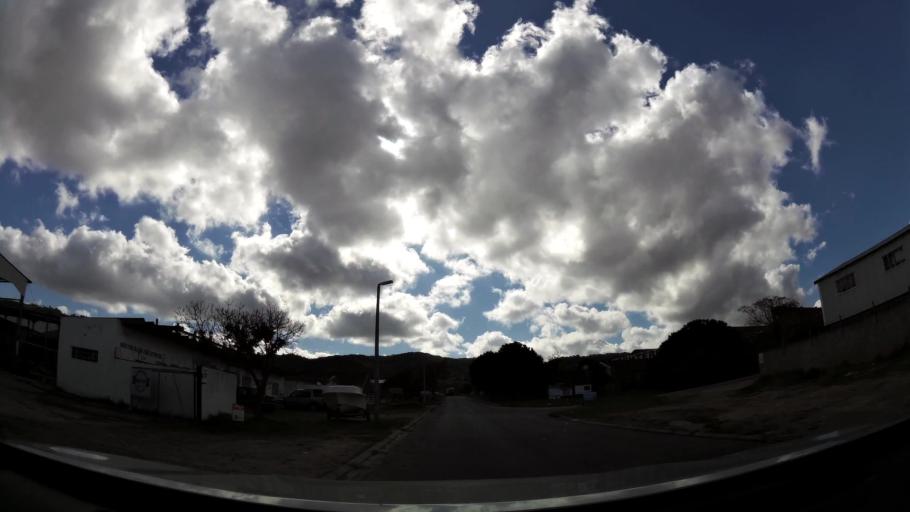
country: ZA
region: Western Cape
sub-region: Eden District Municipality
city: Knysna
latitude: -34.0464
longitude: 23.0759
